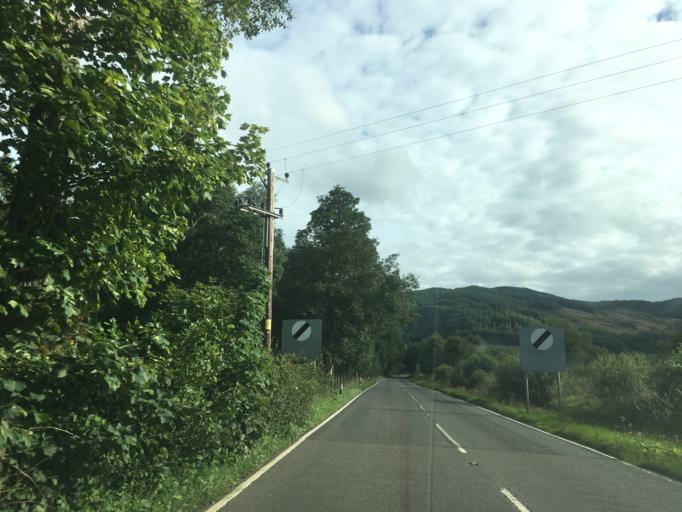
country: GB
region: Scotland
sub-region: Argyll and Bute
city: Oban
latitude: 56.3718
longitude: -5.4384
